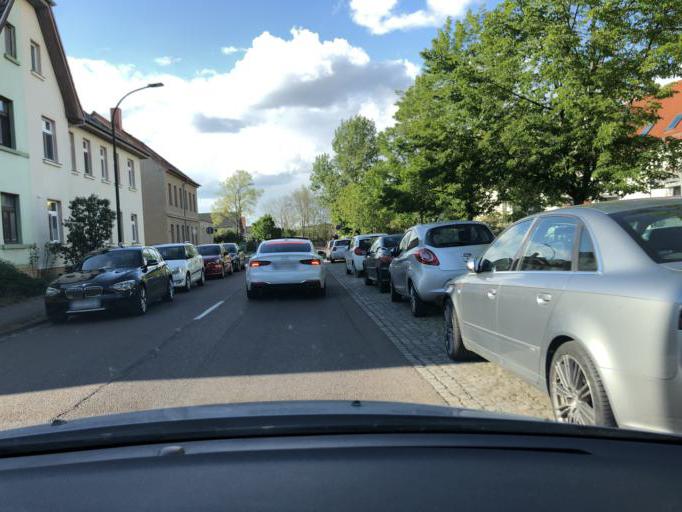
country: DE
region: Saxony
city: Markkleeberg
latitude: 51.2646
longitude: 12.3772
